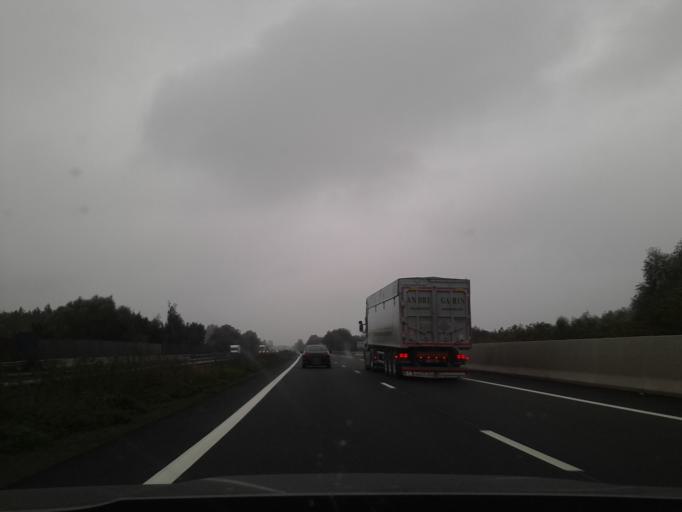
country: FR
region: Nord-Pas-de-Calais
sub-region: Departement du Nord
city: Quarouble
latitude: 50.3959
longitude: 3.6148
